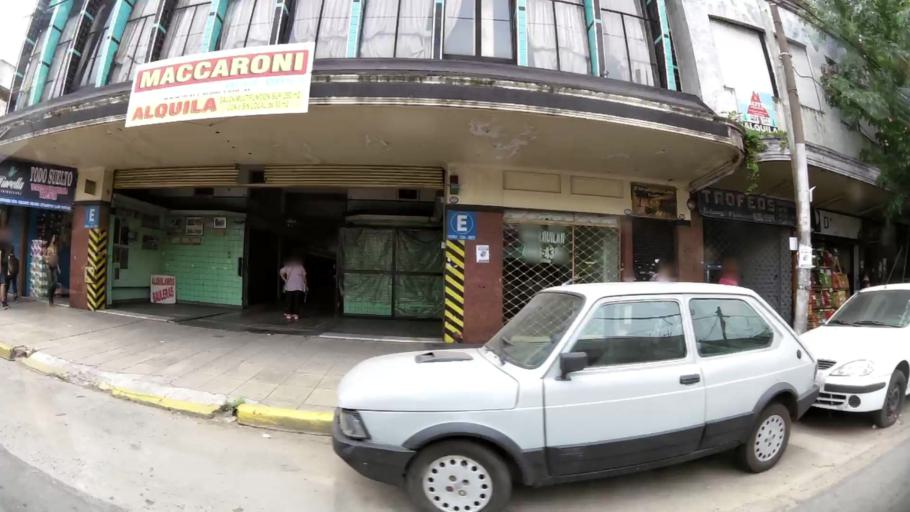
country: AR
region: Buenos Aires
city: San Justo
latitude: -34.6684
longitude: -58.5333
